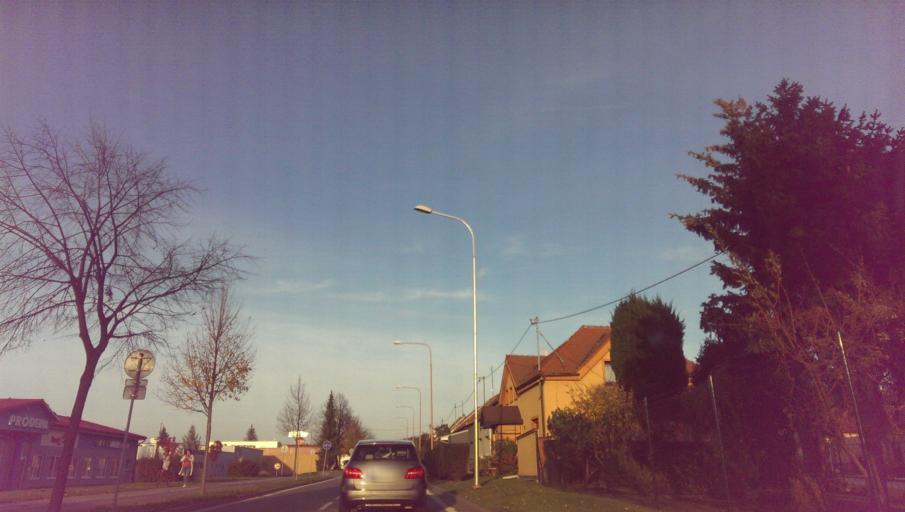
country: CZ
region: Zlin
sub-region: Okres Uherske Hradiste
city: Uherske Hradiste
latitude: 49.0702
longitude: 17.4769
